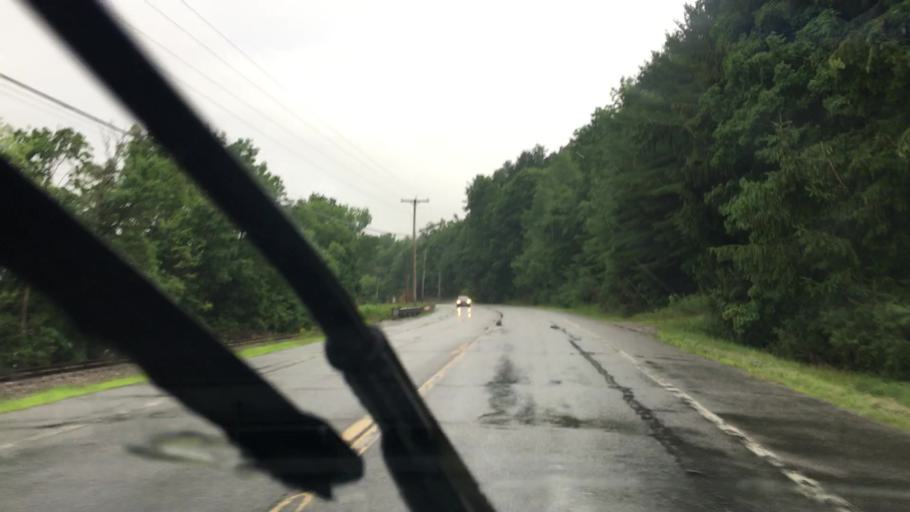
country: US
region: Maine
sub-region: Kennebec County
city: Pittston
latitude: 44.2072
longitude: -69.7648
